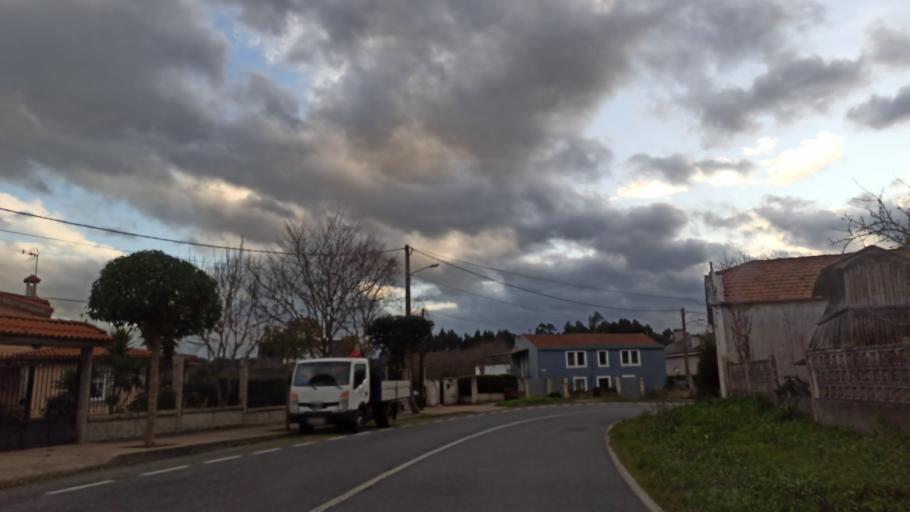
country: ES
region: Galicia
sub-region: Provincia da Coruna
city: Oleiros
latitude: 43.3828
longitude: -8.3226
